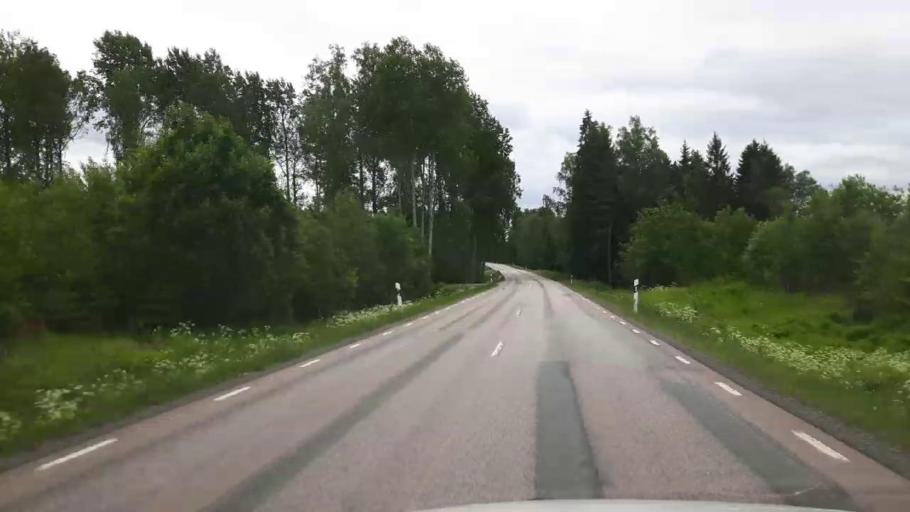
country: SE
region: Vaestmanland
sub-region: Kopings Kommun
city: Kolsva
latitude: 59.6365
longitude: 15.7973
